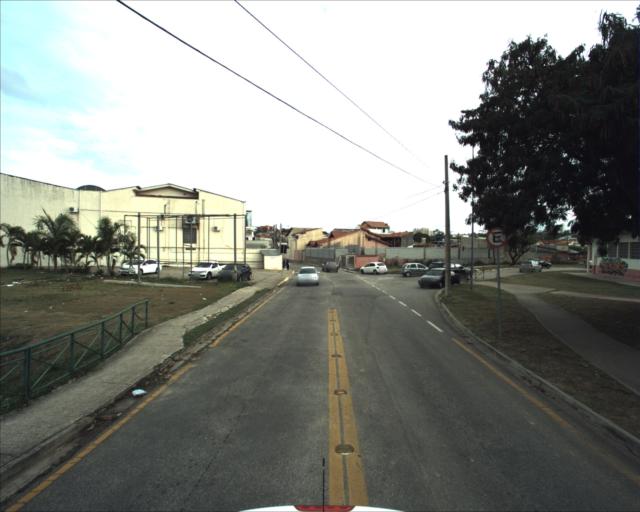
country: BR
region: Sao Paulo
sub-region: Sorocaba
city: Sorocaba
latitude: -23.5154
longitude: -47.4430
